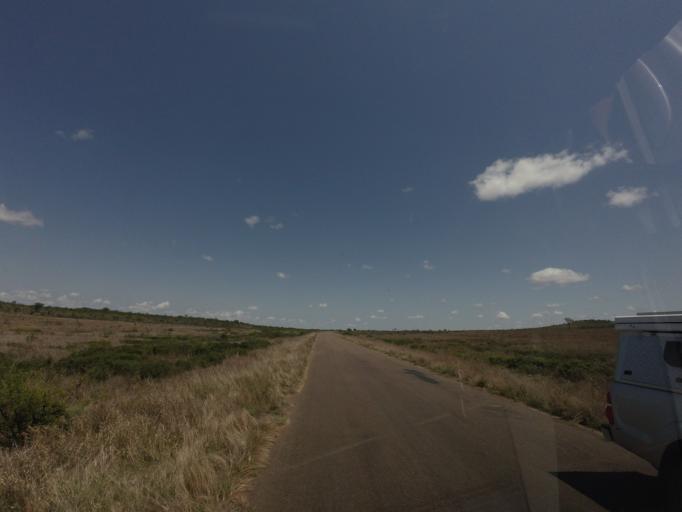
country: ZA
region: Mpumalanga
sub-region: Ehlanzeni District
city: Komatipoort
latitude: -24.8900
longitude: 31.9078
